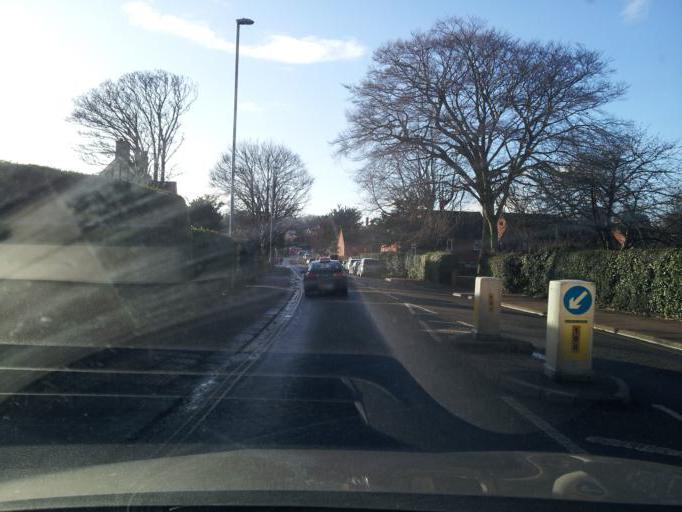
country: GB
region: England
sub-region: Norfolk
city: Cromer
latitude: 52.9254
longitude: 1.3075
